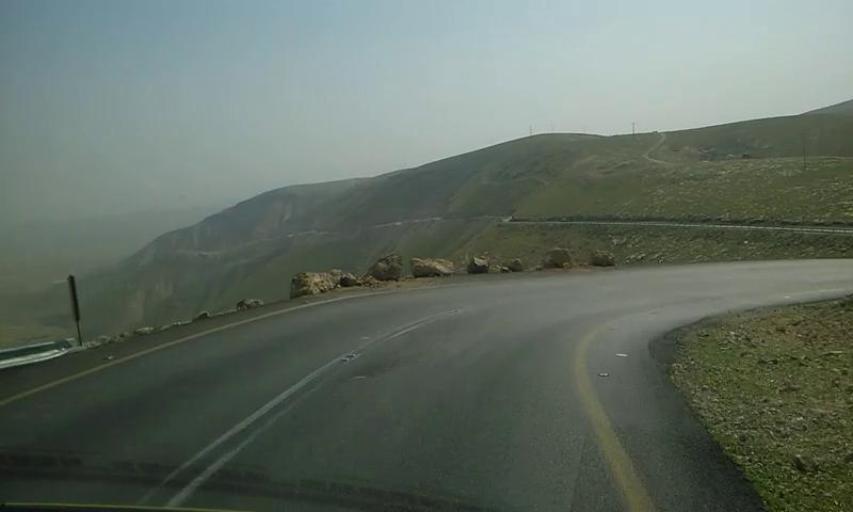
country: PS
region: West Bank
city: Rammun
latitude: 31.9114
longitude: 35.3645
